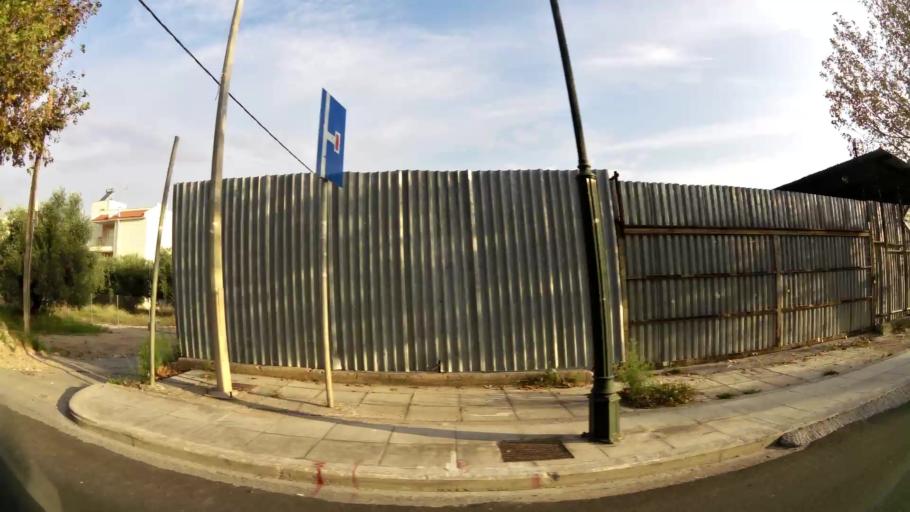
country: GR
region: Attica
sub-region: Nomarchia Dytikis Attikis
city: Ano Liosia
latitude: 38.0704
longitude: 23.7019
